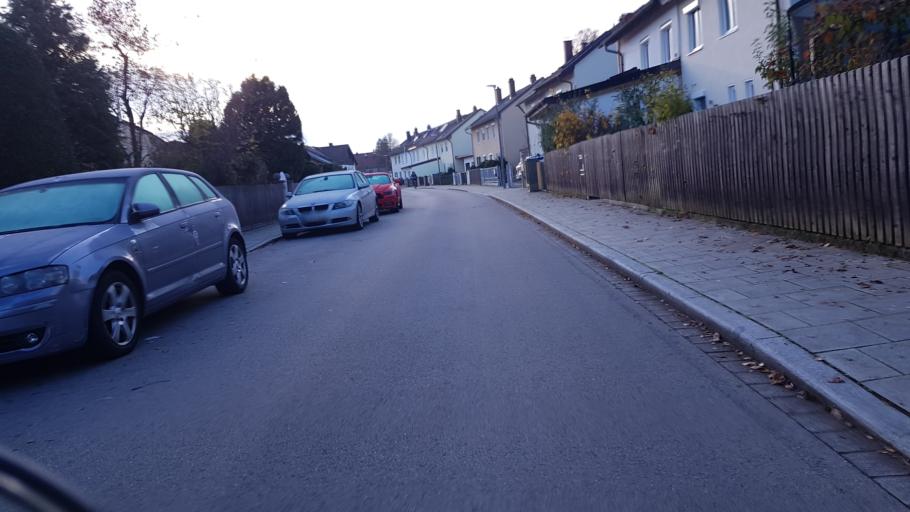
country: DE
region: Bavaria
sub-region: Upper Bavaria
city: Unterhaching
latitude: 48.0792
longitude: 11.6007
